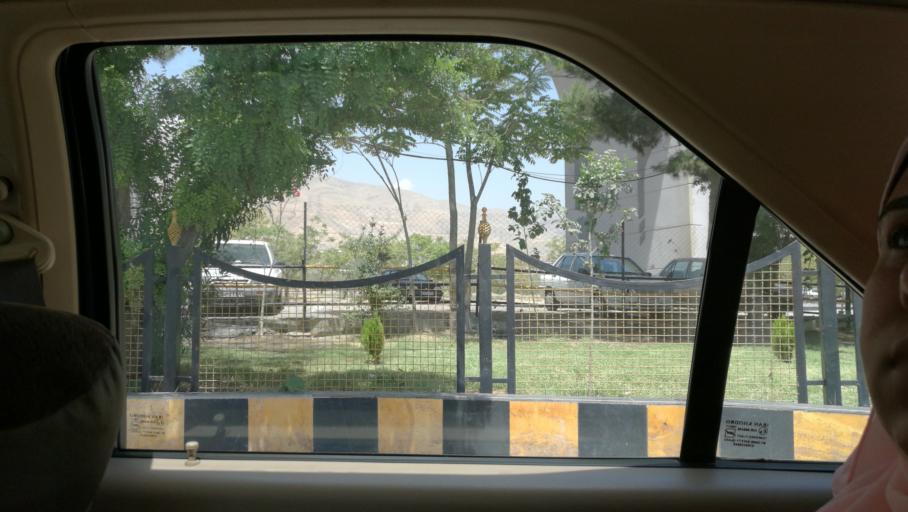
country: IR
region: Tehran
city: Shahr-e Qods
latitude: 35.7453
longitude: 51.1405
